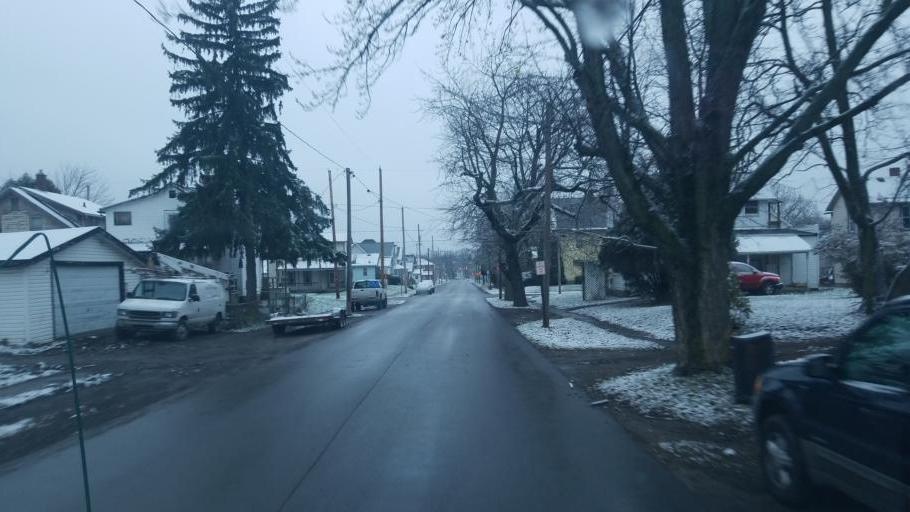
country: US
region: Ohio
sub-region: Marion County
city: Marion
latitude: 40.5950
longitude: -83.1248
